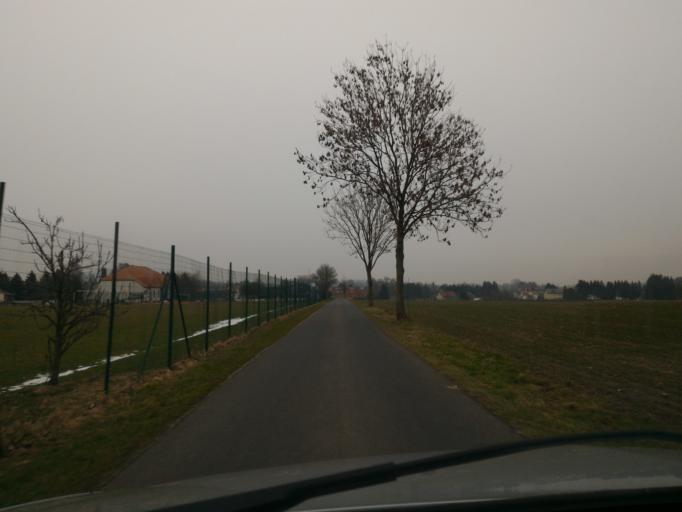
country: DE
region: Saxony
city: Leutersdorf
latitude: 50.9588
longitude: 14.6421
